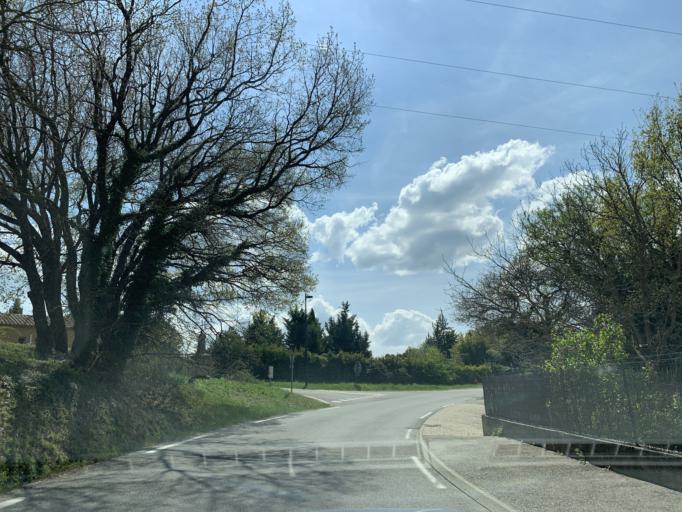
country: FR
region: Provence-Alpes-Cote d'Azur
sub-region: Departement du Vaucluse
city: Goult
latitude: 43.8654
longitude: 5.2488
